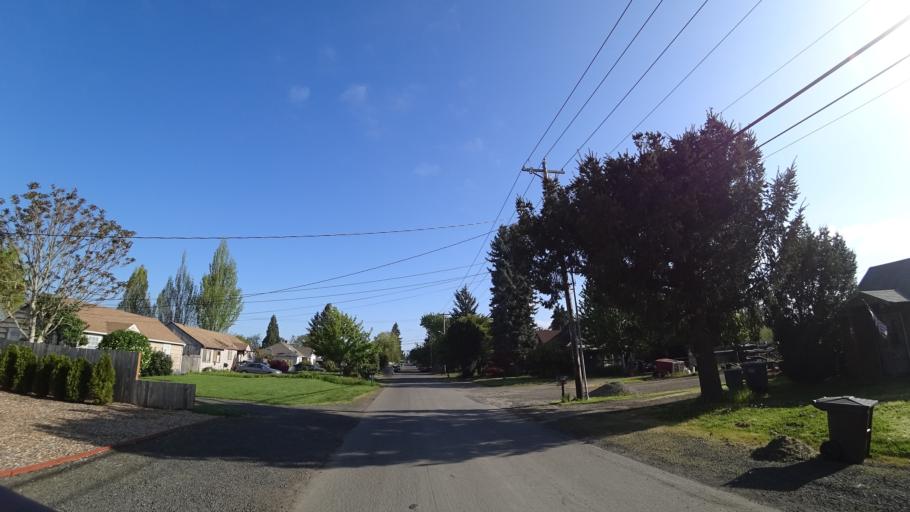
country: US
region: Oregon
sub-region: Washington County
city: Hillsboro
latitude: 45.5145
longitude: -122.9959
